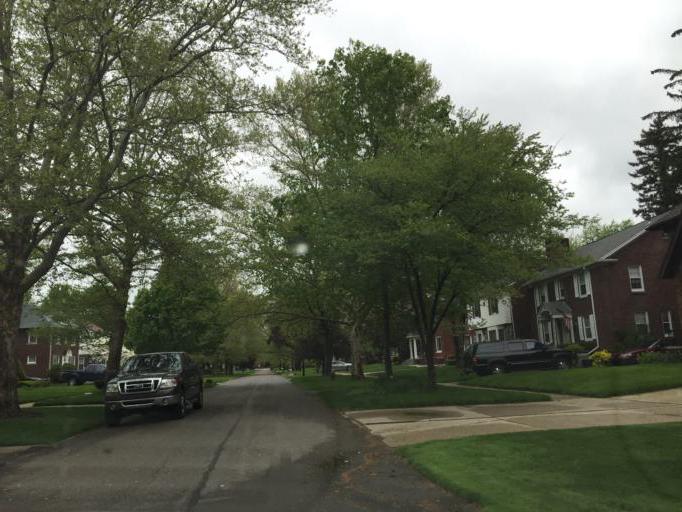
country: US
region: Michigan
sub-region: Oakland County
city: Southfield
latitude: 42.4120
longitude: -83.2330
